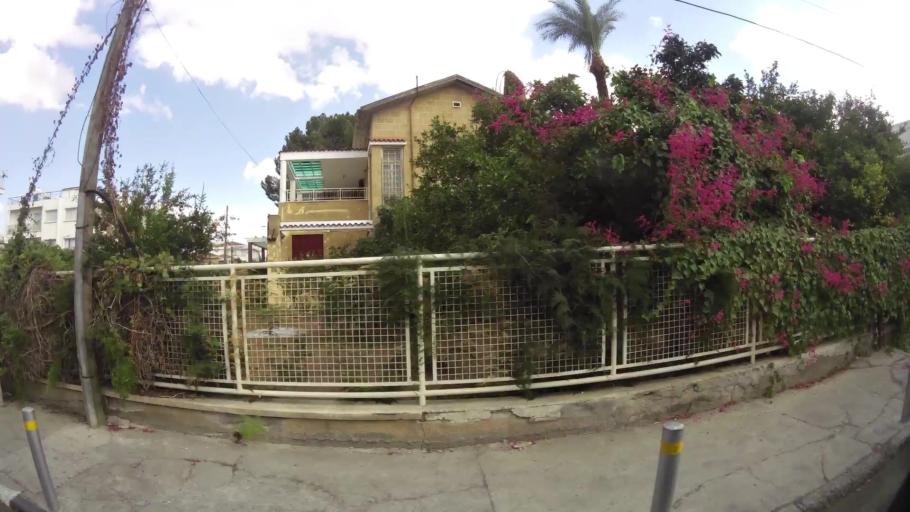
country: CY
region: Lefkosia
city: Nicosia
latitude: 35.1823
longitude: 33.3544
